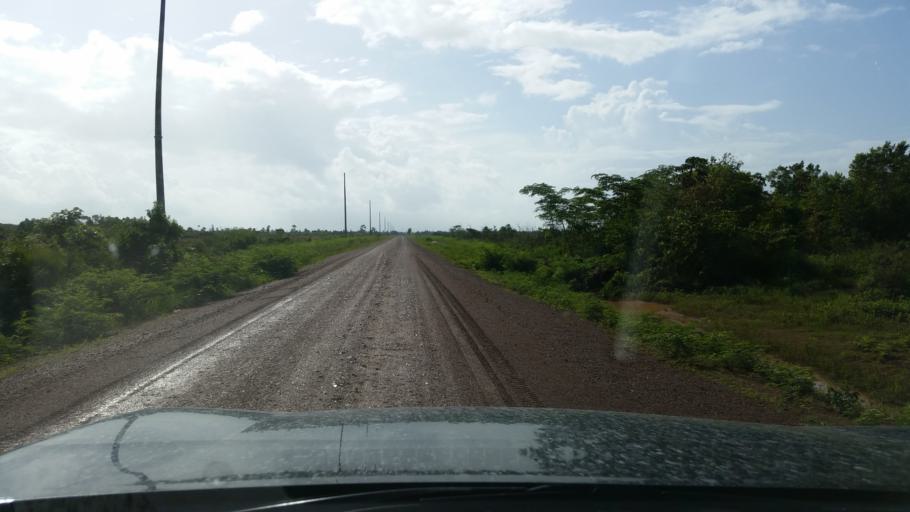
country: NI
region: Atlantico Norte (RAAN)
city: Puerto Cabezas
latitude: 14.1091
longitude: -83.5840
